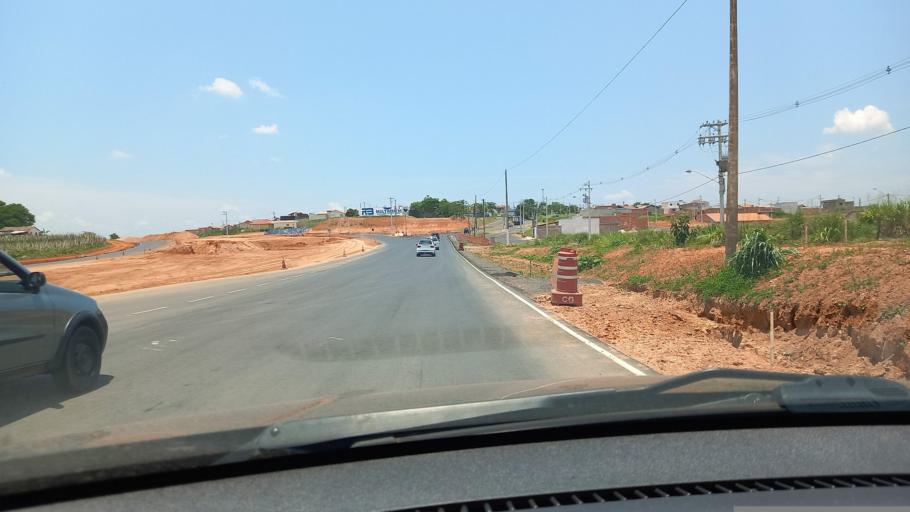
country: BR
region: Sao Paulo
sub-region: Itapira
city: Itapira
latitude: -22.4055
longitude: -46.8443
